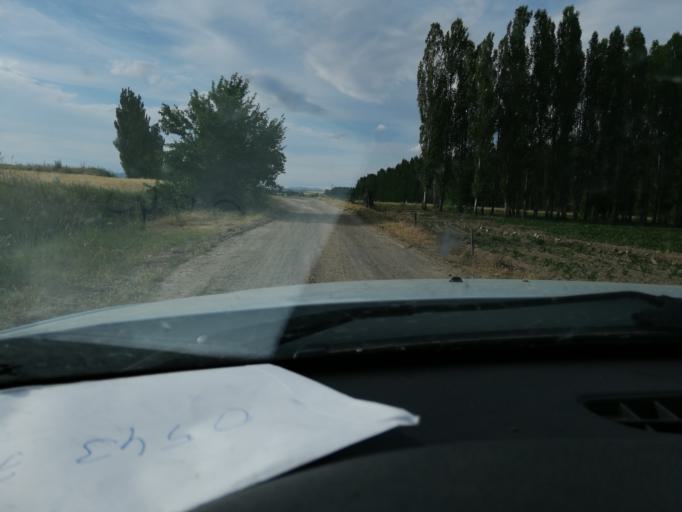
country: TR
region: Kirsehir
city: Kirsehir
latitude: 39.0025
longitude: 34.1238
